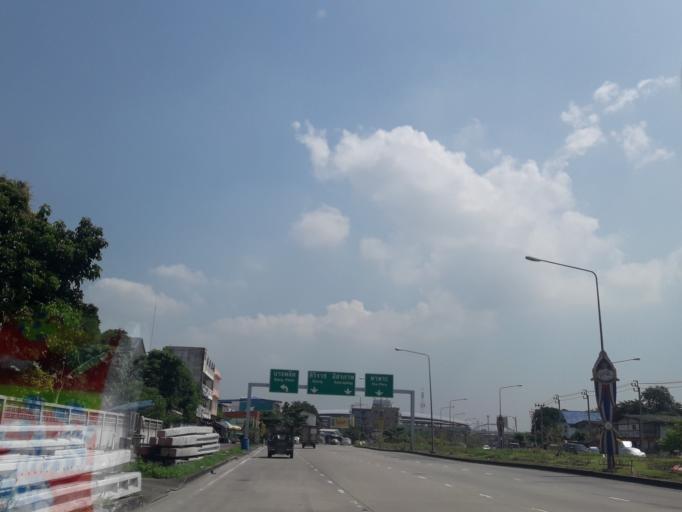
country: TH
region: Bangkok
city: Bangkok Noi
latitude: 13.7550
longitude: 100.4635
